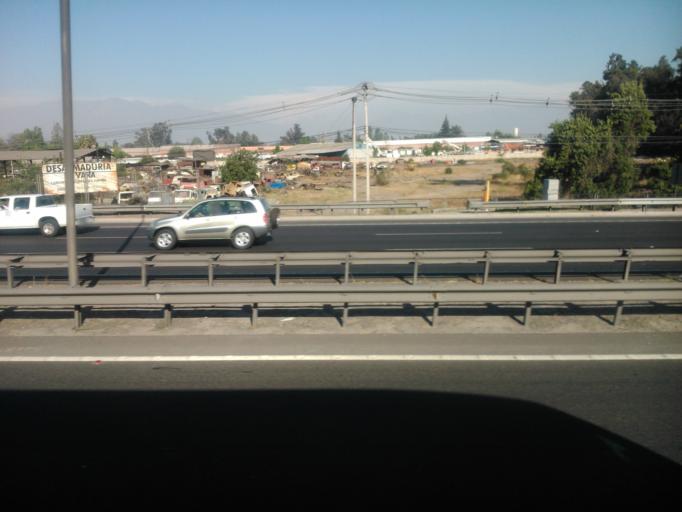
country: CL
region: Santiago Metropolitan
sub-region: Provincia de Maipo
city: San Bernardo
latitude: -33.5683
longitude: -70.7119
